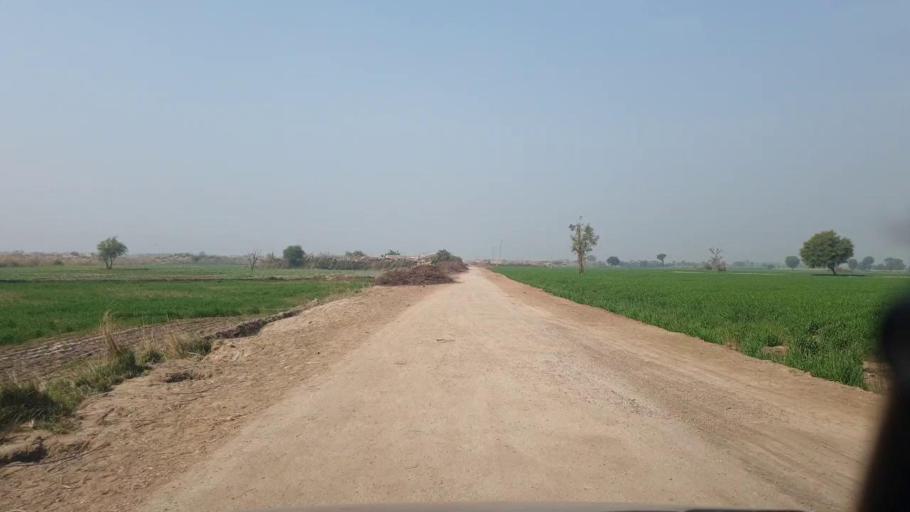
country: PK
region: Sindh
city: Shahdadpur
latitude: 26.0307
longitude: 68.5276
